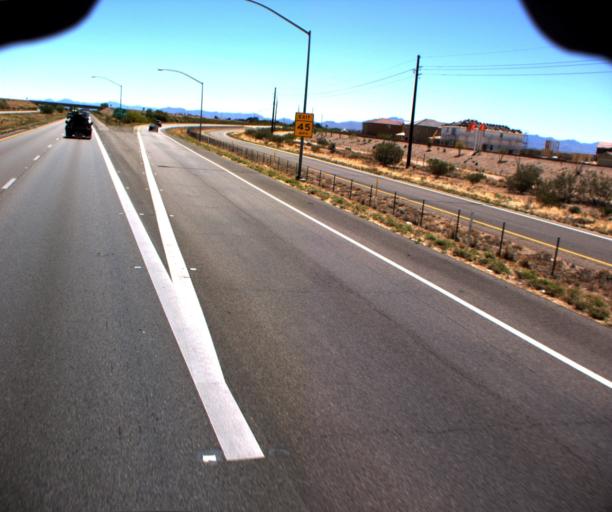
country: US
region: Arizona
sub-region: Pima County
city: Summit
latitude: 32.1075
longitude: -110.8471
